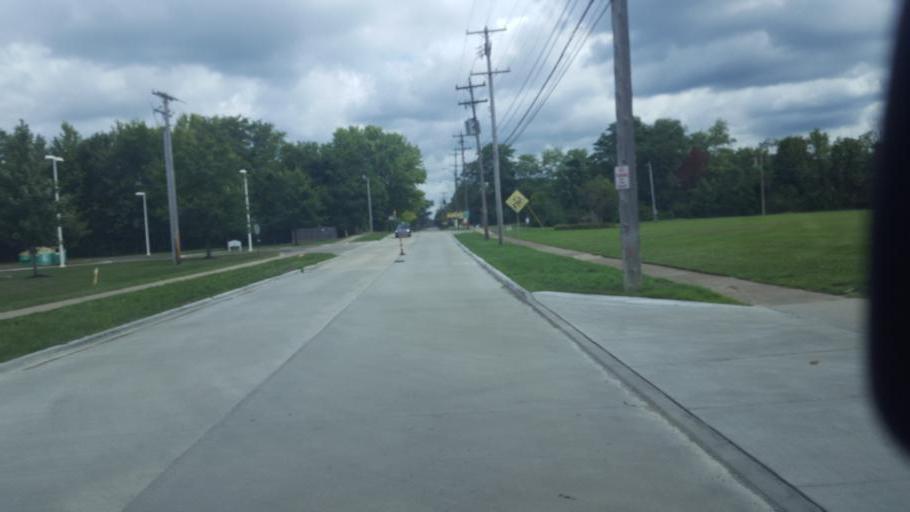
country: US
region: Ohio
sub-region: Lake County
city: Painesville
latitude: 41.7150
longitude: -81.2456
